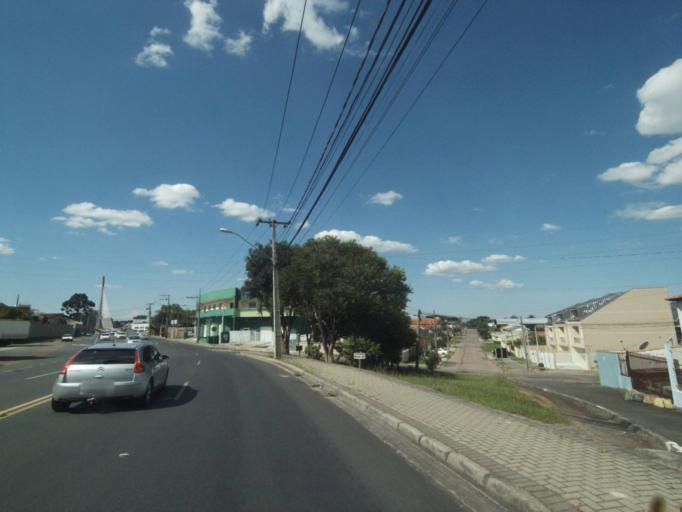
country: BR
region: Parana
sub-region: Pinhais
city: Pinhais
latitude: -25.4691
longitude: -49.2353
